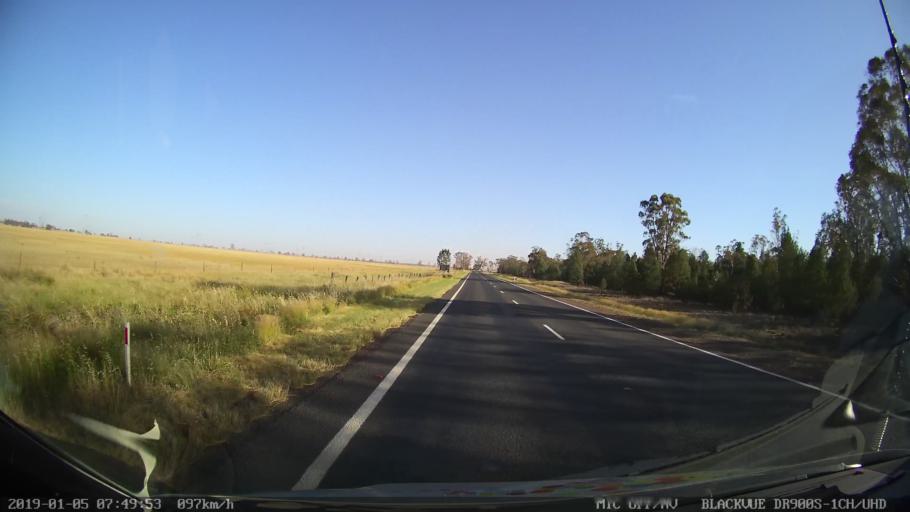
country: AU
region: New South Wales
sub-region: Gilgandra
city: Gilgandra
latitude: -31.7952
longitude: 148.6358
